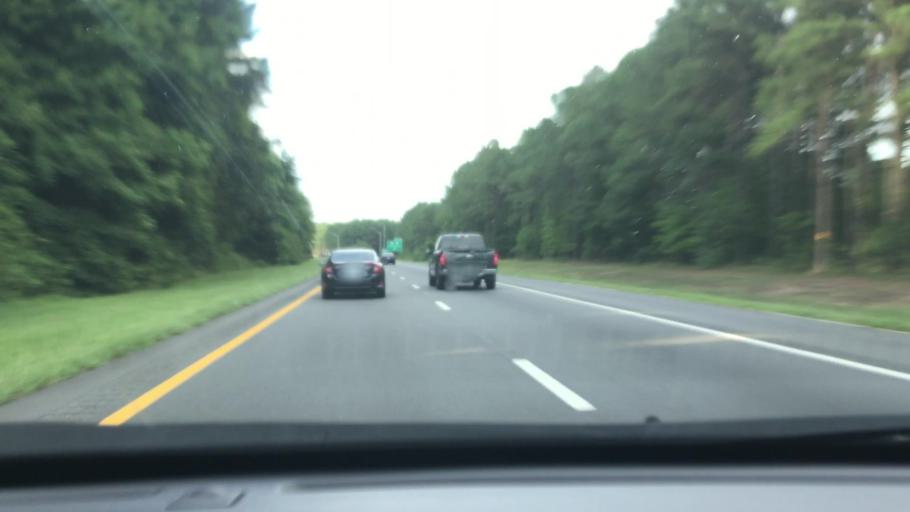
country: US
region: North Carolina
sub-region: Cumberland County
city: Vander
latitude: 35.0011
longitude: -78.8248
